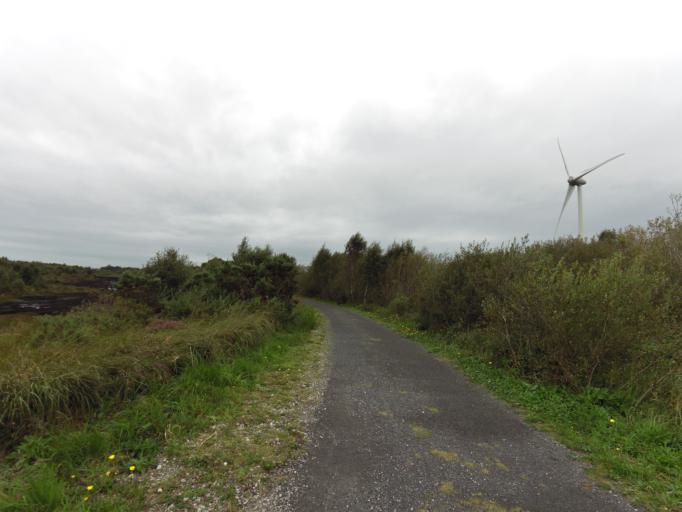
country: IE
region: Leinster
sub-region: Uibh Fhaili
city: Ferbane
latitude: 53.2309
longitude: -7.7672
